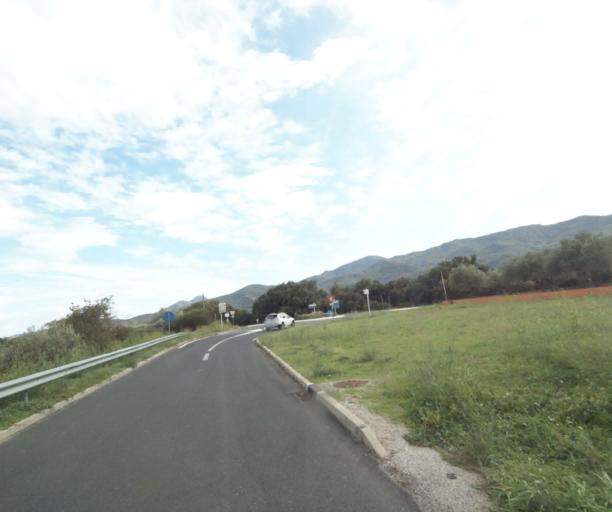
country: FR
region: Languedoc-Roussillon
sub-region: Departement des Pyrenees-Orientales
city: Argelers
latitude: 42.5446
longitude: 3.0088
